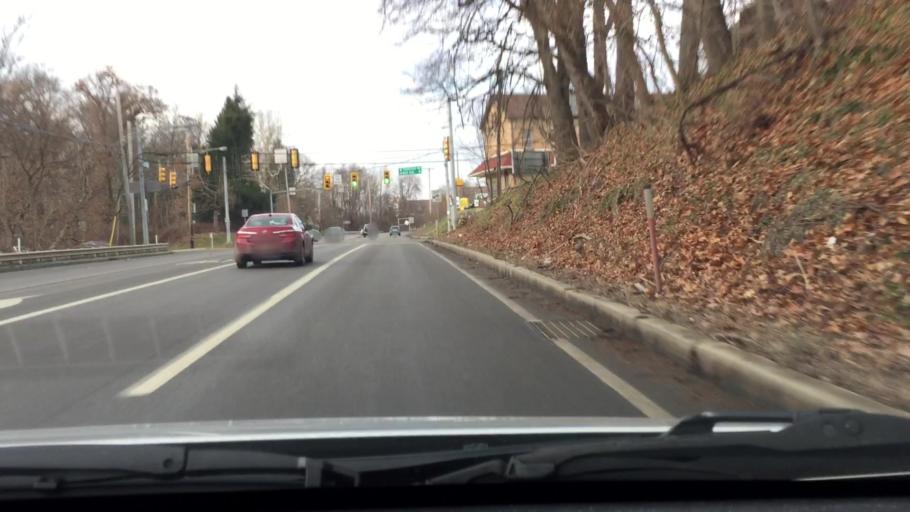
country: US
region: Pennsylvania
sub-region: Beaver County
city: Aliquippa
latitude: 40.6097
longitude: -80.2730
